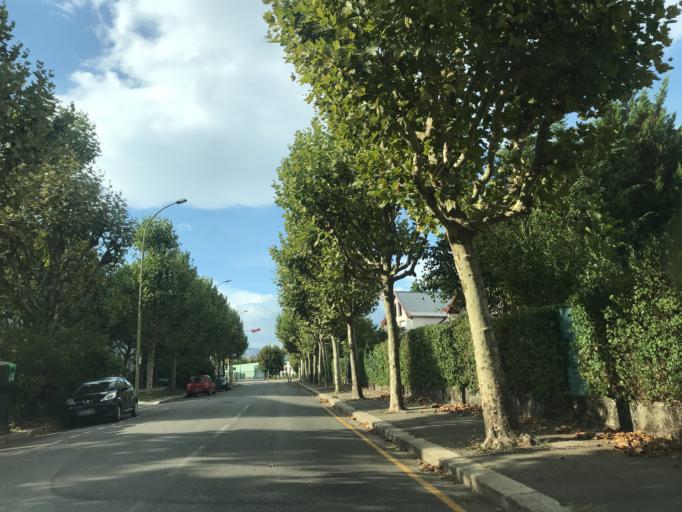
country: FR
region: Rhone-Alpes
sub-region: Departement de la Haute-Savoie
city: Annecy-le-Vieux
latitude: 45.9214
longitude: 6.1309
